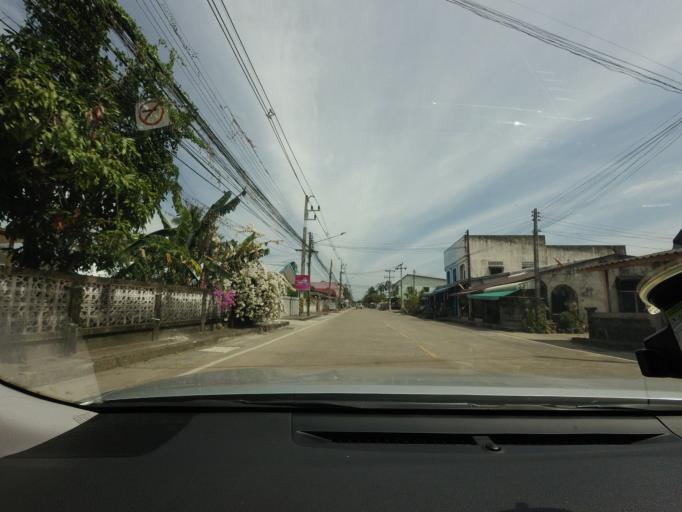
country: TH
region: Narathiwat
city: Narathiwat
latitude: 6.4260
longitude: 101.8128
